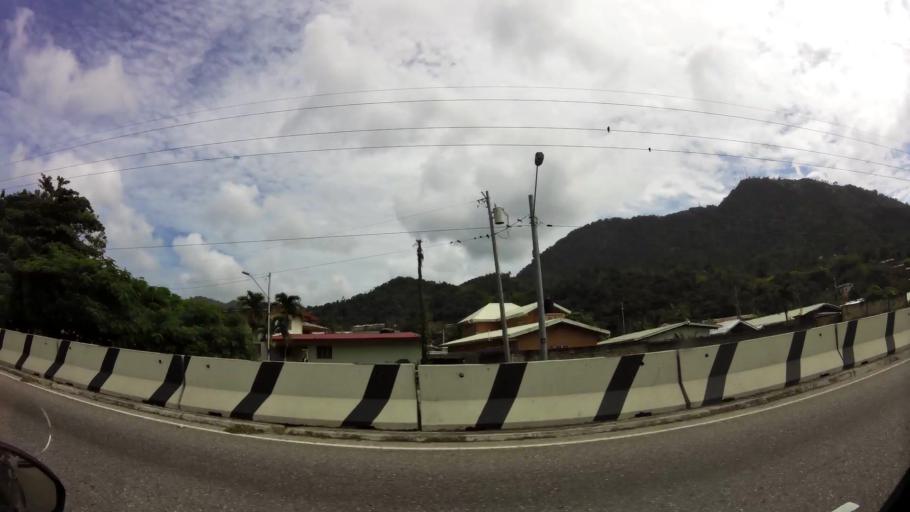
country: TT
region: Diego Martin
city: Petit Valley
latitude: 10.7029
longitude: -61.5533
